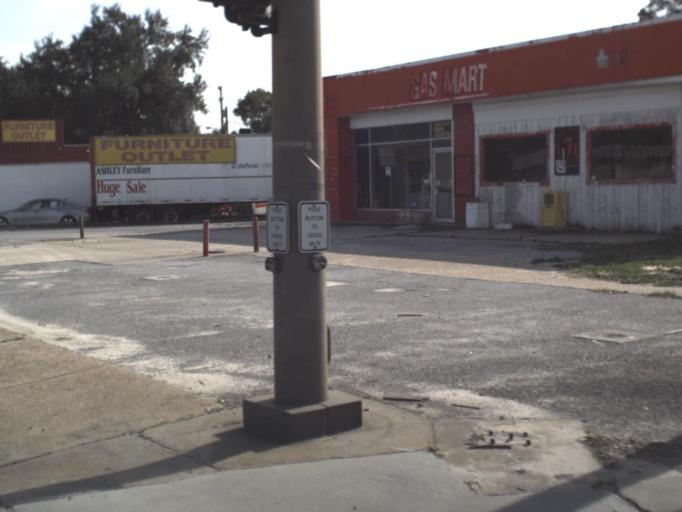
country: US
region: Florida
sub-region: Bay County
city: Springfield
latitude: 30.1531
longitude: -85.6172
